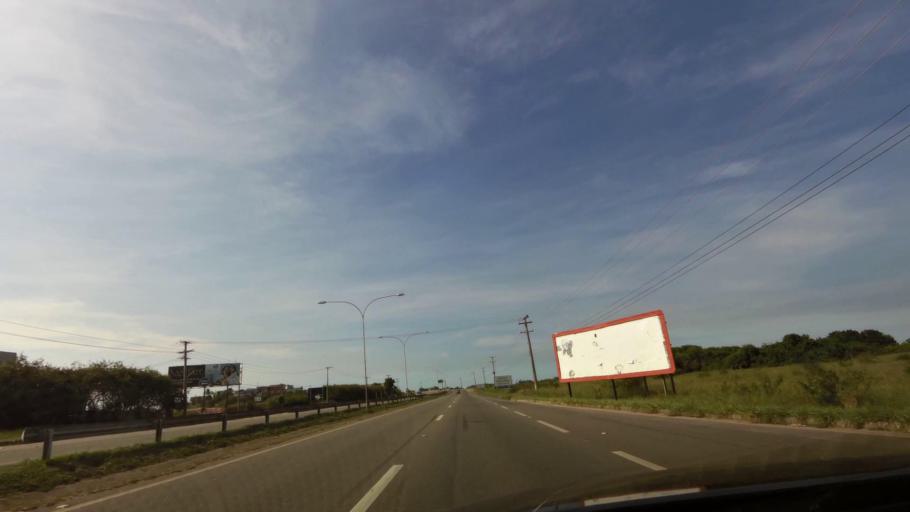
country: BR
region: Espirito Santo
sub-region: Vila Velha
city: Vila Velha
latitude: -20.4534
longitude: -40.3371
